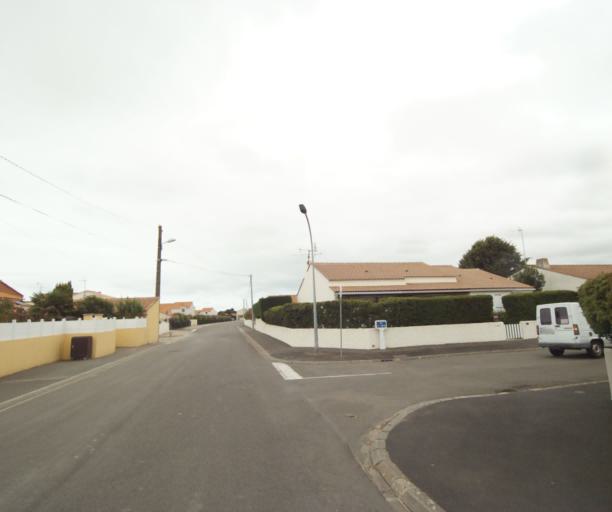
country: FR
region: Pays de la Loire
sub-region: Departement de la Vendee
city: Chateau-d'Olonne
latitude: 46.5002
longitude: -1.7478
